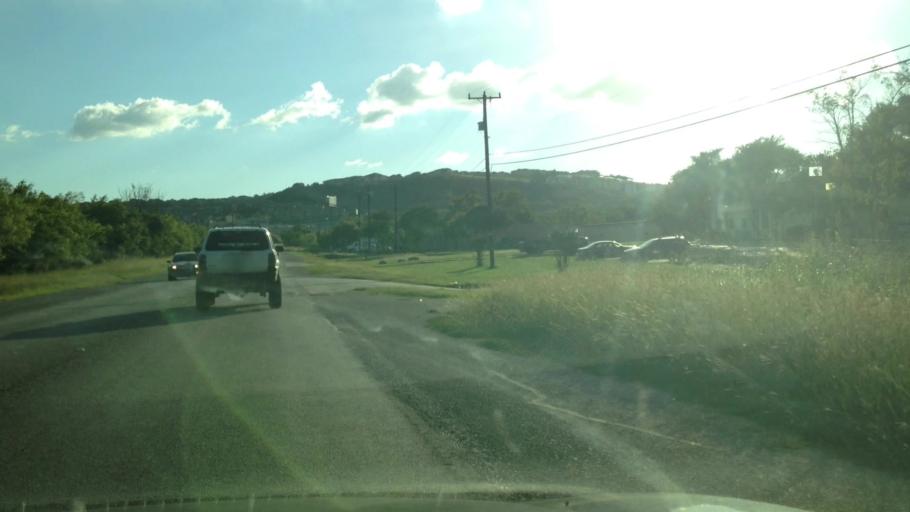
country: US
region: Texas
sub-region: Bexar County
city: Cross Mountain
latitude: 29.6286
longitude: -98.6048
